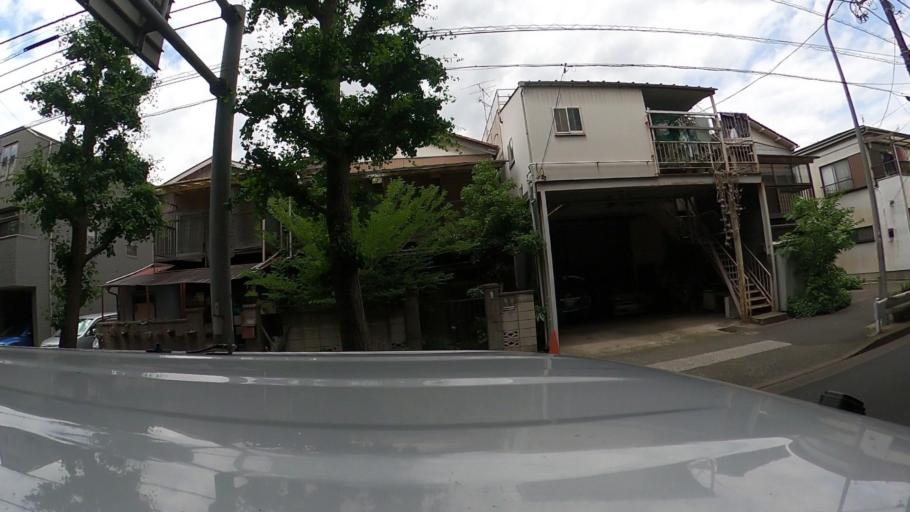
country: JP
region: Kanagawa
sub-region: Kawasaki-shi
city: Kawasaki
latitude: 35.5000
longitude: 139.6931
